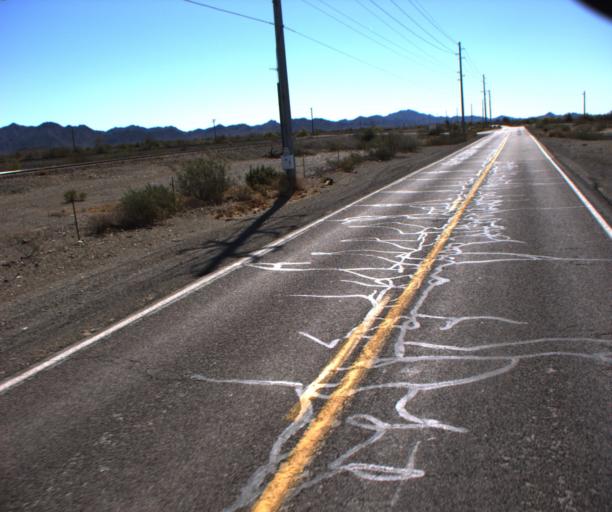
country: US
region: Arizona
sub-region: La Paz County
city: Salome
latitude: 33.7489
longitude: -113.7655
